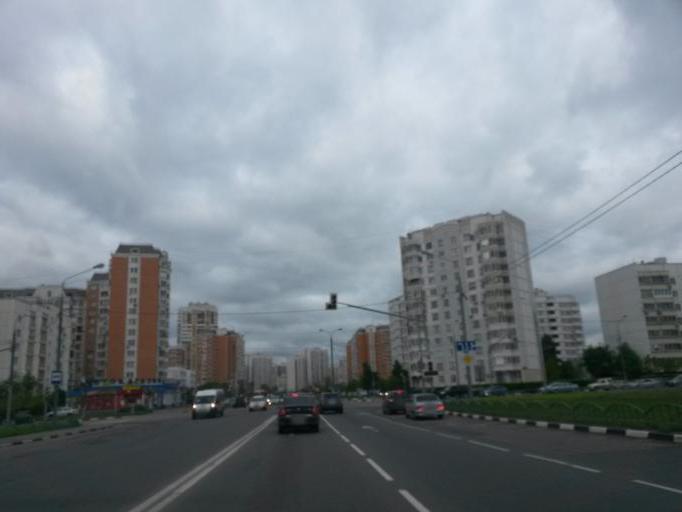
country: RU
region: Moscow
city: Kapotnya
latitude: 55.6602
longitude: 37.7807
